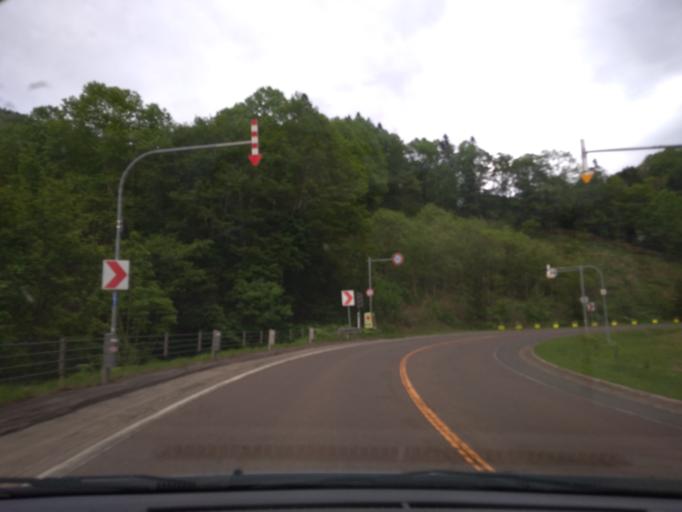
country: JP
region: Hokkaido
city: Shimo-furano
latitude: 43.0924
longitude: 142.4057
